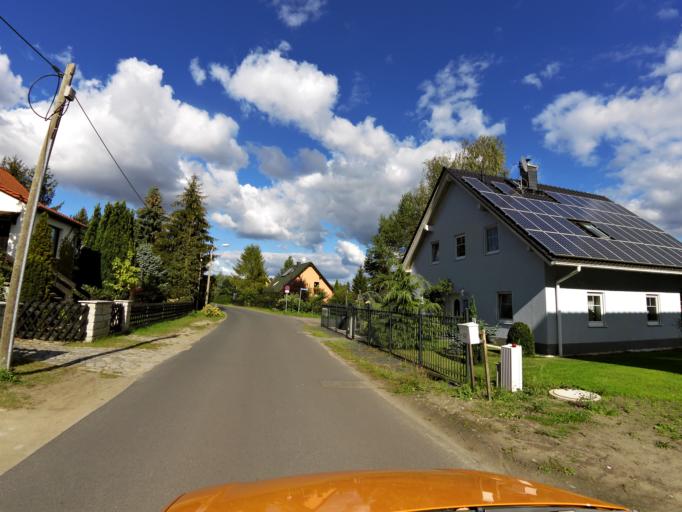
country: DE
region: Brandenburg
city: Luckenwalde
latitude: 52.0767
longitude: 13.1732
